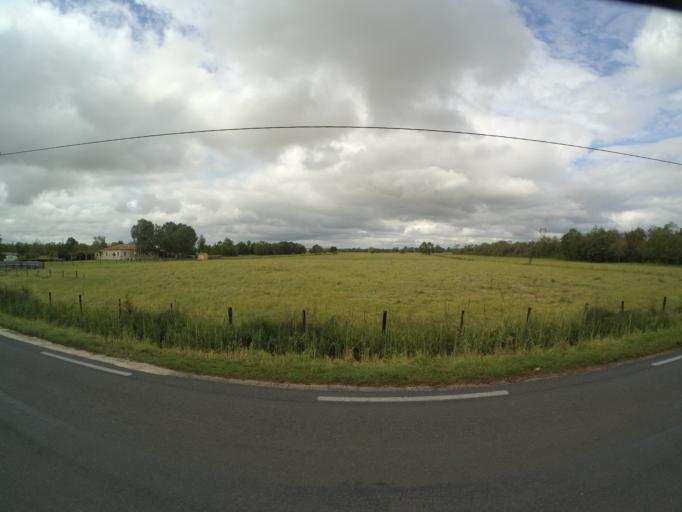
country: FR
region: Aquitaine
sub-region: Departement de la Gironde
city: Ludon-Medoc
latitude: 44.9995
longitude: -0.5975
